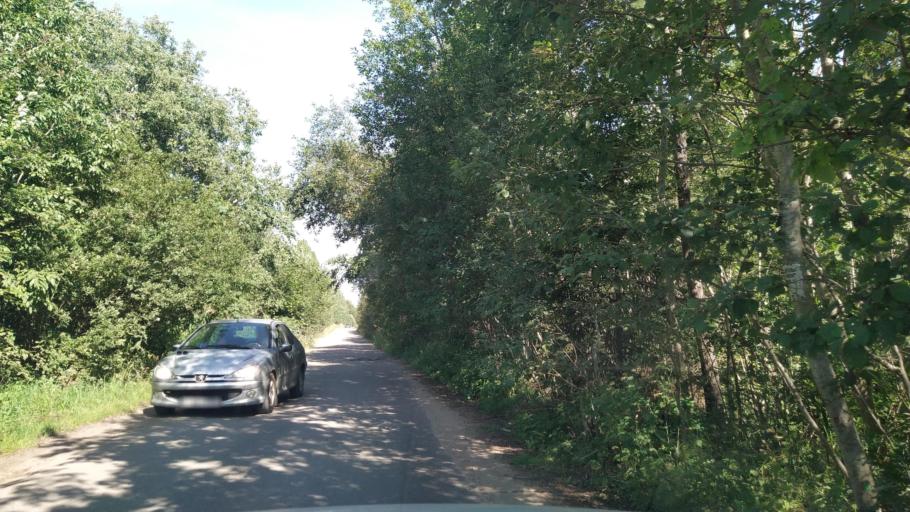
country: RU
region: Leningrad
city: Siverskiy
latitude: 59.2815
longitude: 30.0290
